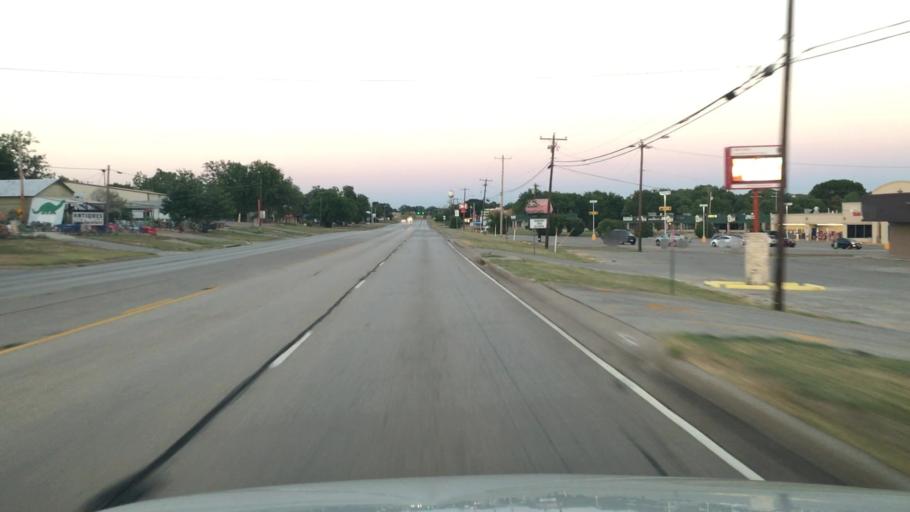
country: US
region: Texas
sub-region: Somervell County
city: Glen Rose
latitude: 32.2337
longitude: -97.7686
